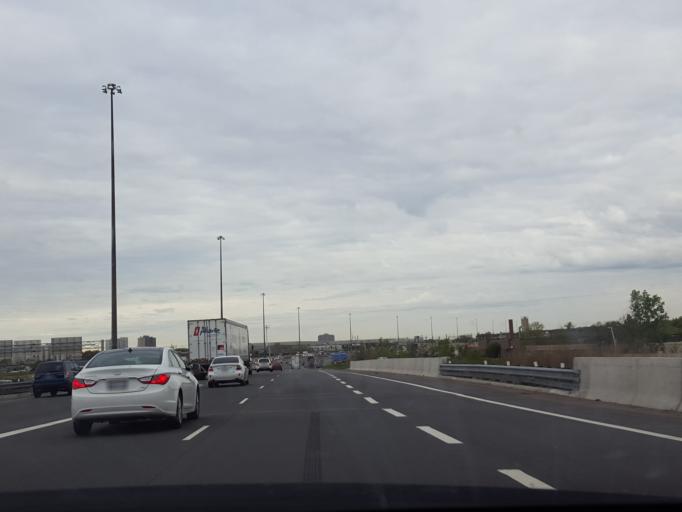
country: CA
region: Ontario
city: Etobicoke
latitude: 43.7179
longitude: -79.5192
